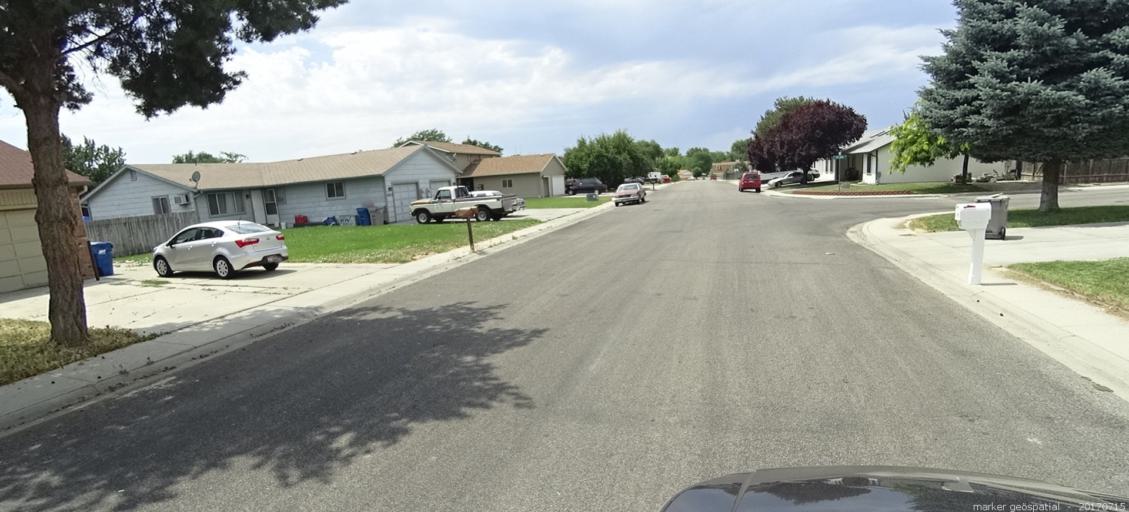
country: US
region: Idaho
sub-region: Ada County
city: Garden City
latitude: 43.5689
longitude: -116.3093
